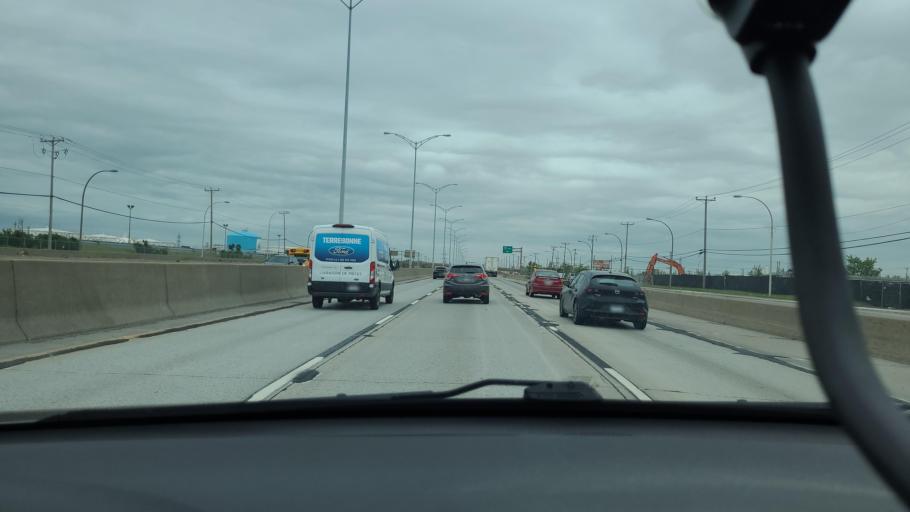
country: CA
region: Quebec
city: Montreal-Est
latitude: 45.6383
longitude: -73.5372
